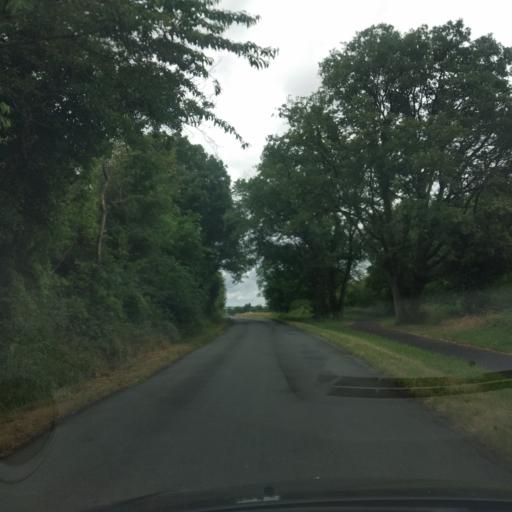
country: FR
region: Poitou-Charentes
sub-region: Departement de la Vienne
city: Vouneuil-sous-Biard
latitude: 46.5936
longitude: 0.2724
